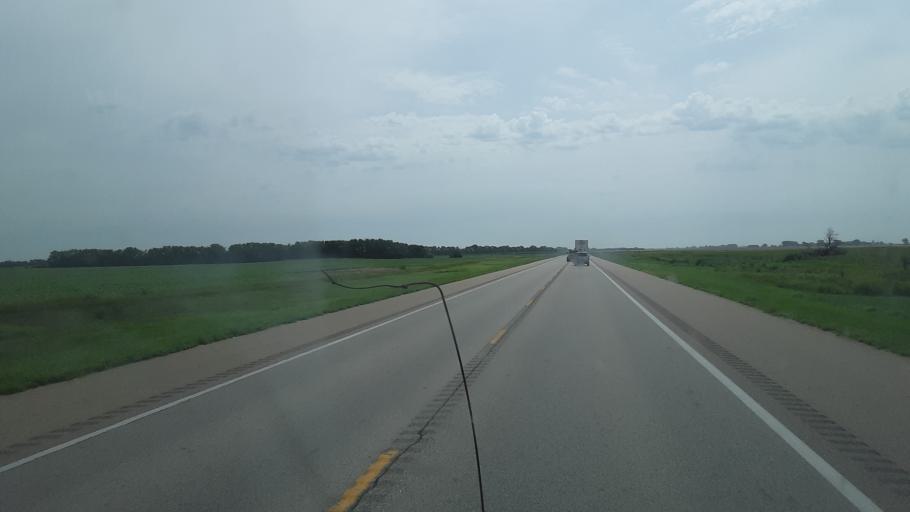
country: US
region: Kansas
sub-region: Reno County
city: Nickerson
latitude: 37.9850
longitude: -98.2205
